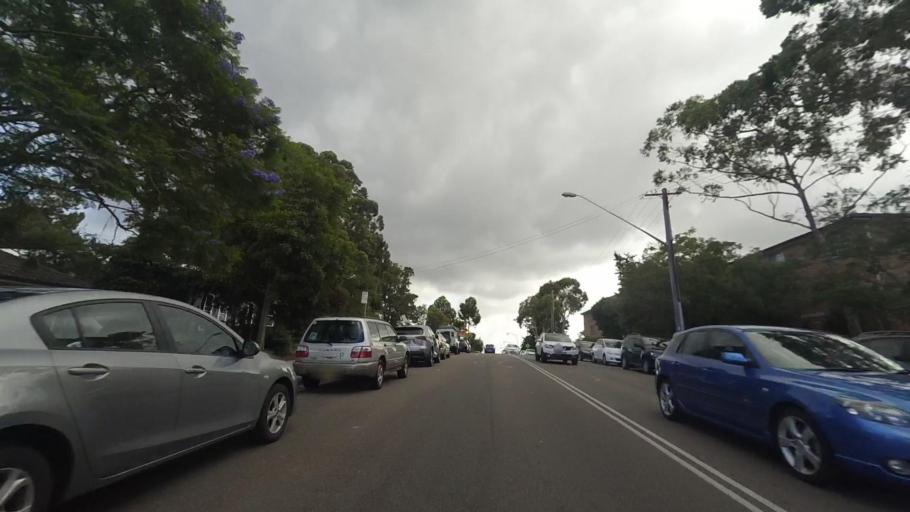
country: AU
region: New South Wales
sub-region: Sutherland Shire
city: Engadine
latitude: -34.0671
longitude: 151.0113
